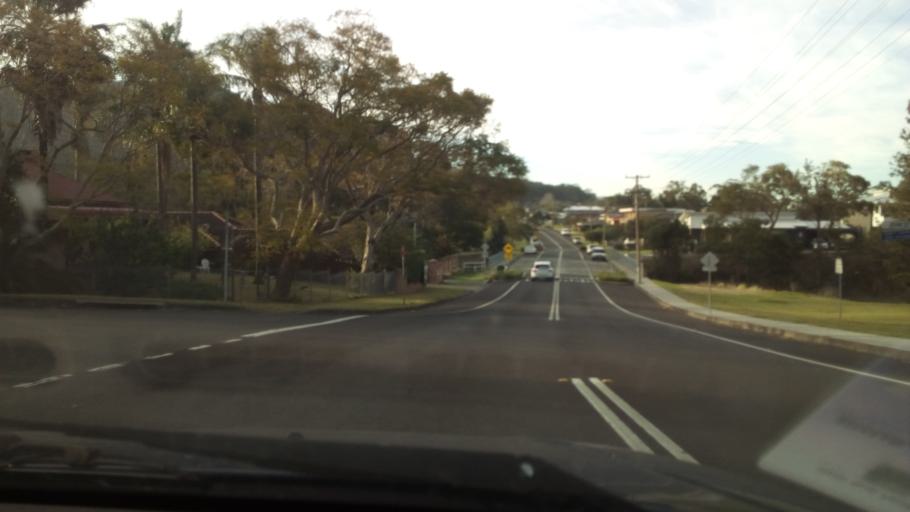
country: AU
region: New South Wales
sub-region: Wollongong
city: Mount Ousley
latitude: -34.3871
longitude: 150.8809
